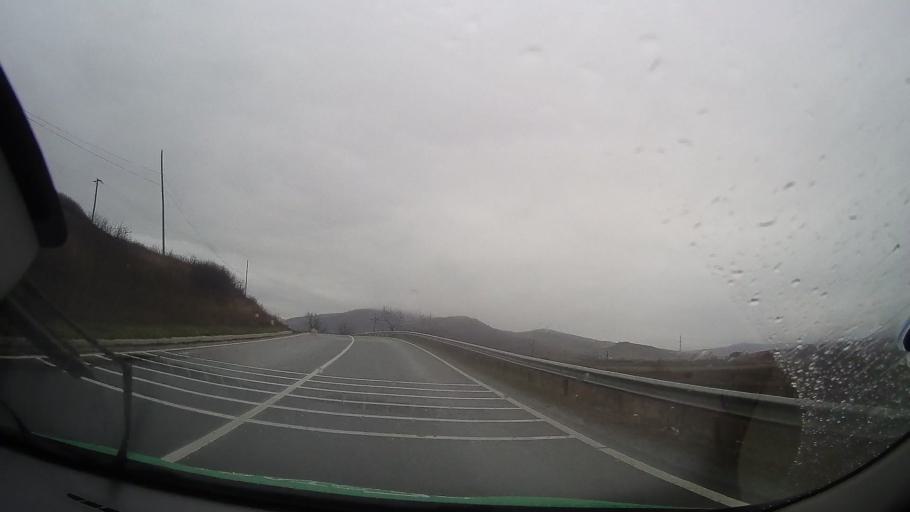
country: RO
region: Bistrita-Nasaud
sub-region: Comuna Galatii Bistritei
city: Galatii Bistritei
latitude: 46.9550
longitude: 24.4442
